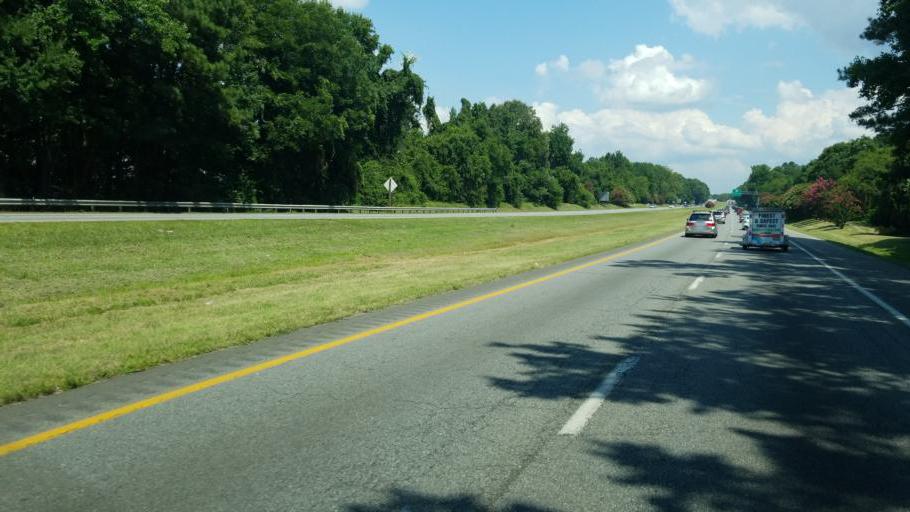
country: US
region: Virginia
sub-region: City of Suffolk
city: Suffolk
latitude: 36.7652
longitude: -76.5772
